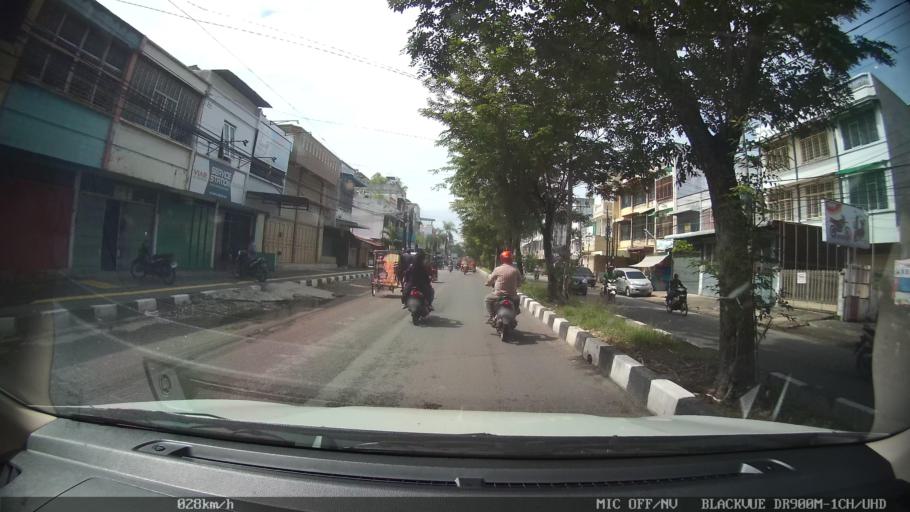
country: ID
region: North Sumatra
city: Medan
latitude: 3.5936
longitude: 98.7060
